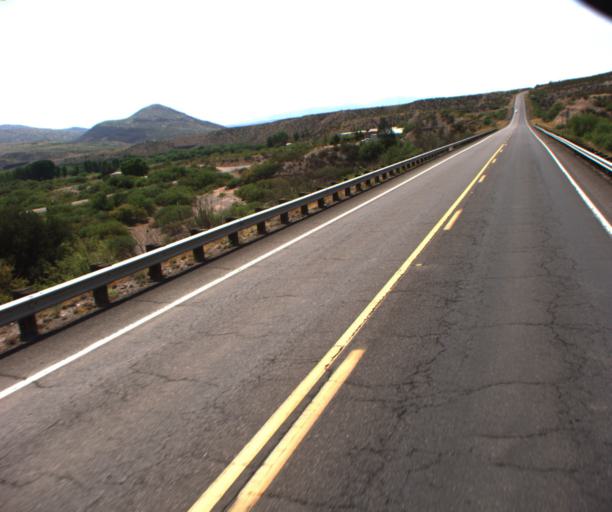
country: US
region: Arizona
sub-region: Greenlee County
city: Clifton
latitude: 32.9393
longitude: -109.2197
